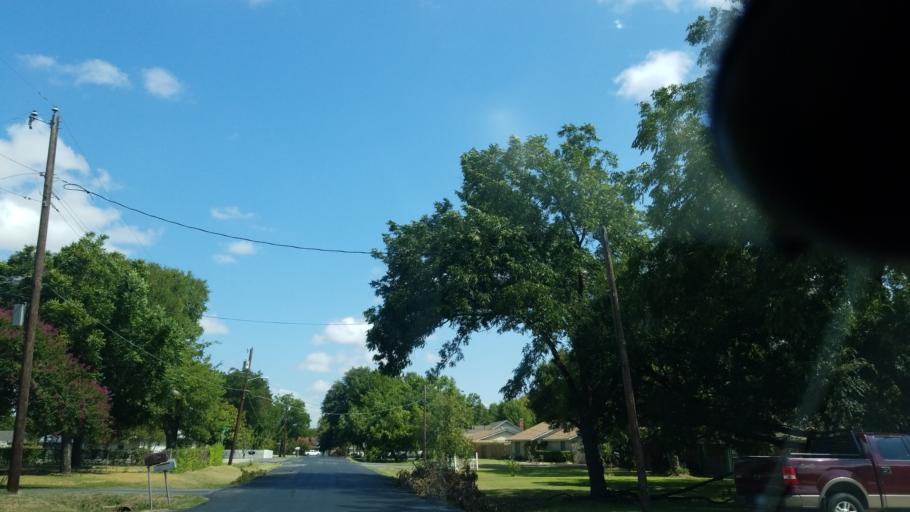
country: US
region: Texas
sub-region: Dallas County
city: Grand Prairie
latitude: 32.7107
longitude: -96.9964
